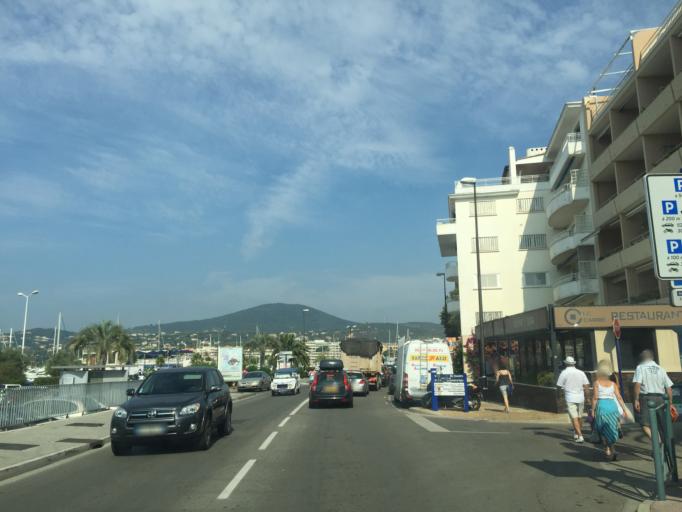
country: FR
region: Provence-Alpes-Cote d'Azur
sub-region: Departement du Var
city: Sainte-Maxime
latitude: 43.3064
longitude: 6.6420
